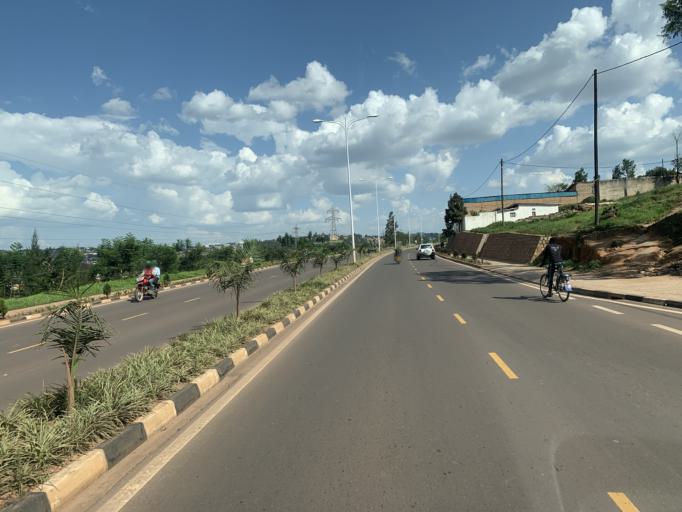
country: RW
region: Kigali
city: Kigali
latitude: -1.9641
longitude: 30.0790
